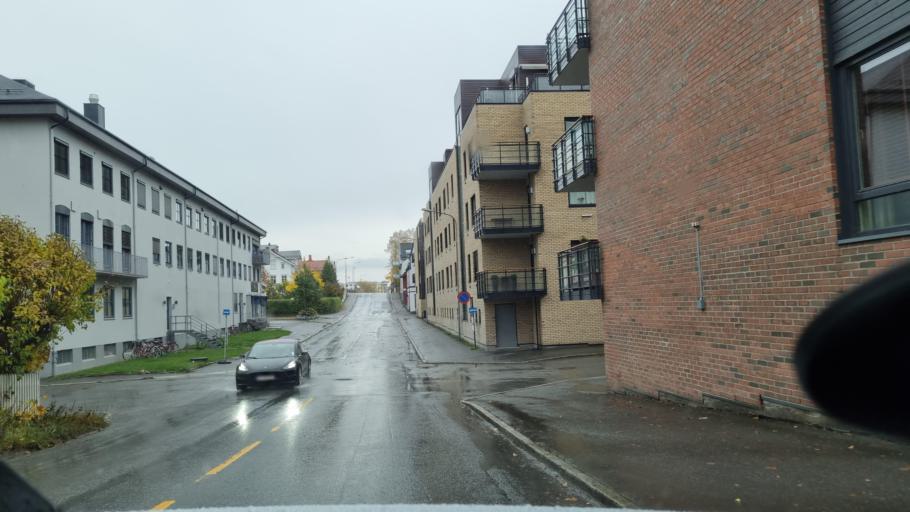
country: NO
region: Hedmark
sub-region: Hamar
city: Hamar
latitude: 60.7961
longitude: 11.0606
